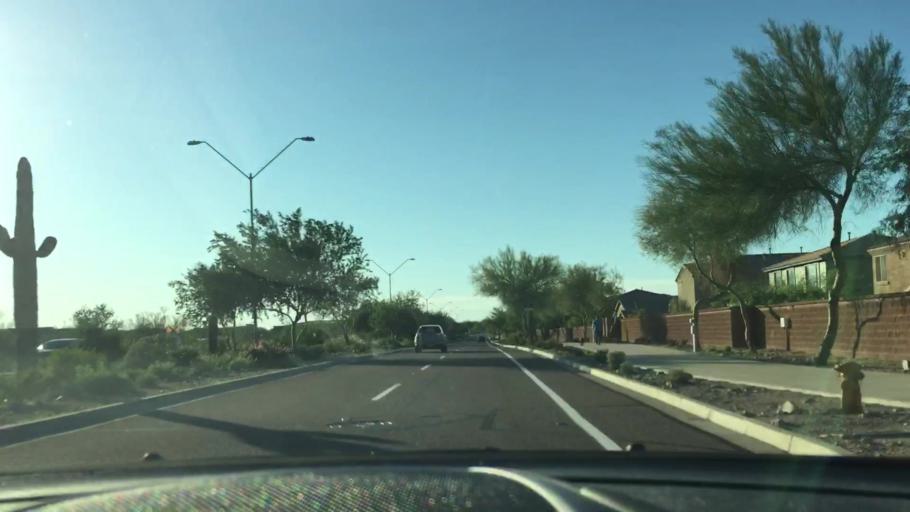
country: US
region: Arizona
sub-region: Maricopa County
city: Sun City West
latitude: 33.7292
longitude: -112.2462
